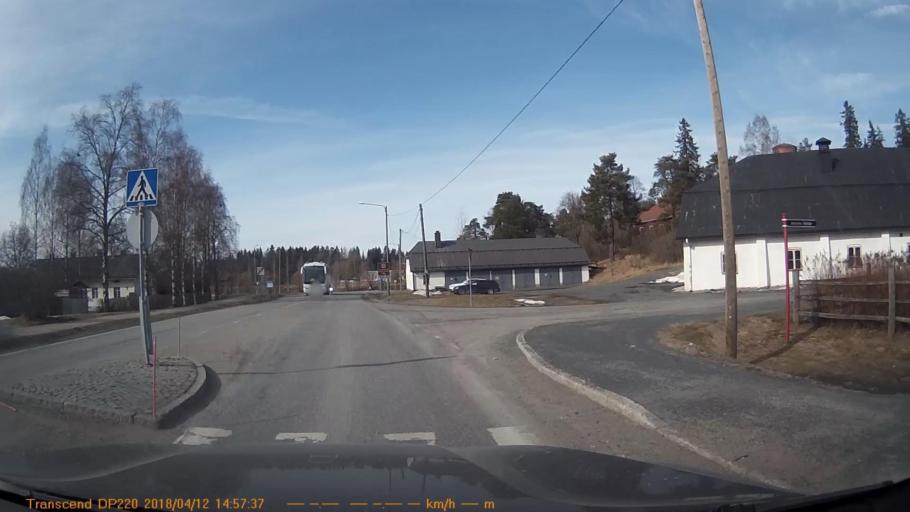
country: FI
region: Haeme
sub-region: Forssa
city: Jokioinen
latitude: 60.8059
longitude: 23.4853
